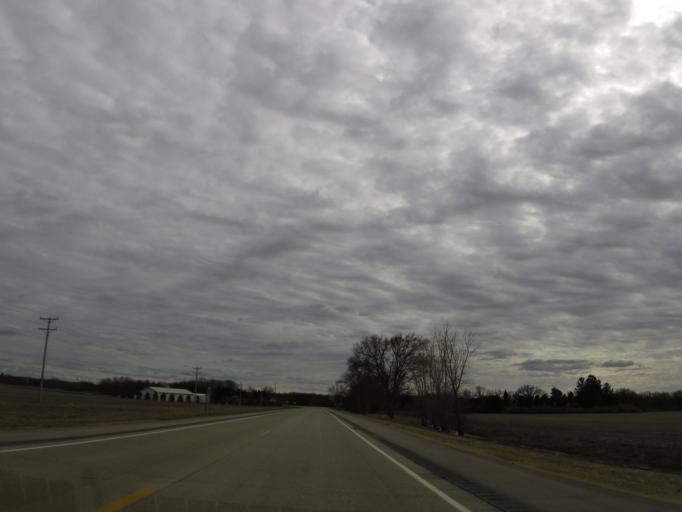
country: US
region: Minnesota
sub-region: Fillmore County
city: Spring Valley
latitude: 43.5051
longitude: -92.3693
